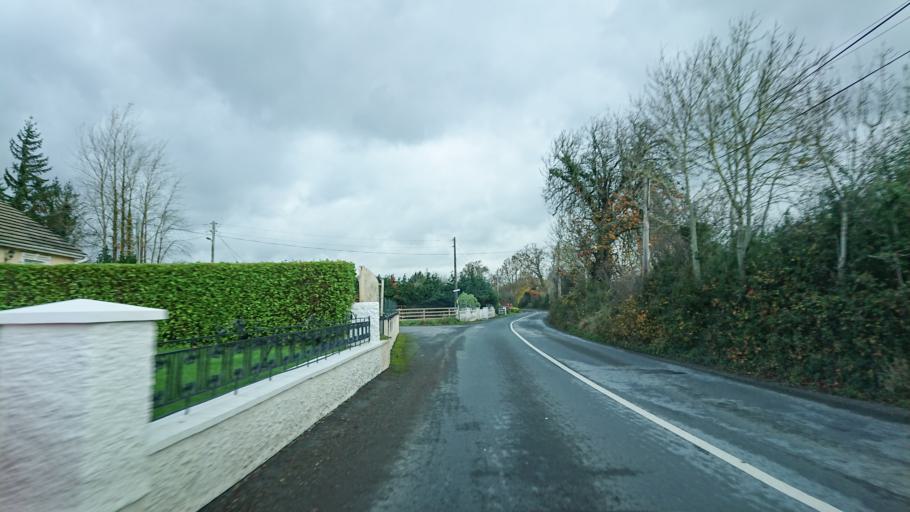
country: IE
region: Munster
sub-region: South Tipperary
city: Cluain Meala
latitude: 52.3568
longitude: -7.6601
